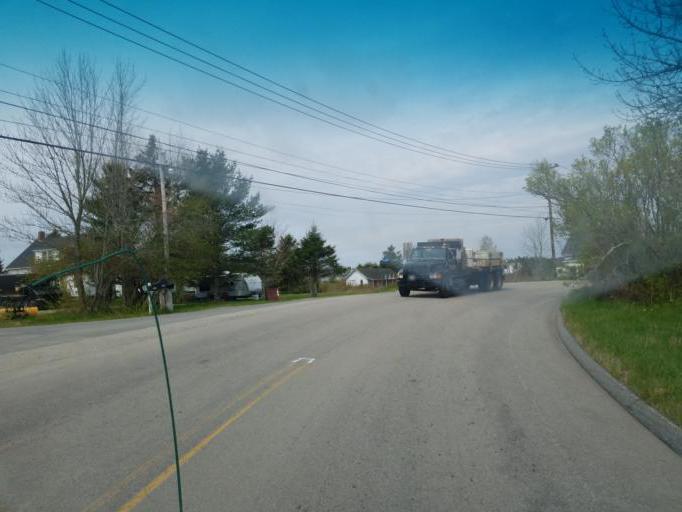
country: US
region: Maine
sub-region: Washington County
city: Eastport
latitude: 44.7887
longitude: -67.1738
